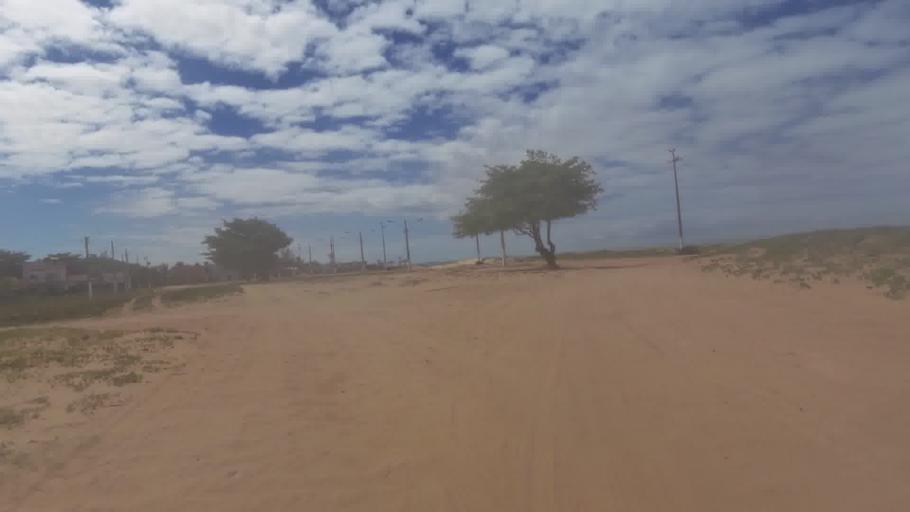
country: BR
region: Espirito Santo
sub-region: Marataizes
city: Marataizes
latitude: -21.1924
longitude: -40.9291
